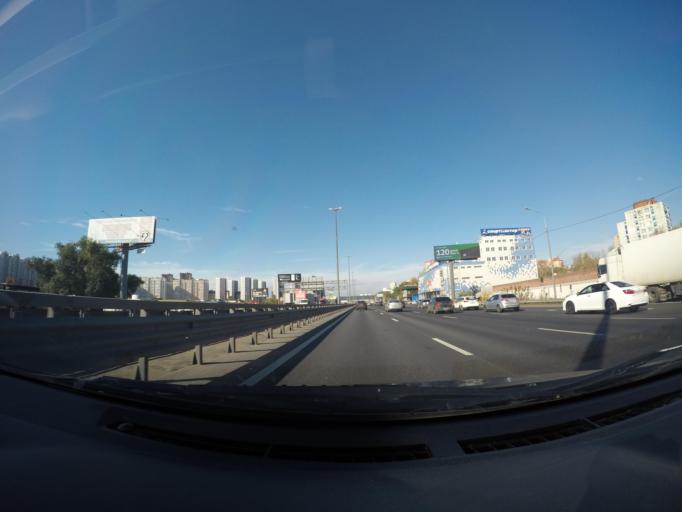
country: RU
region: Moskovskaya
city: Lyubertsy
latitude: 55.6686
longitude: 37.8727
